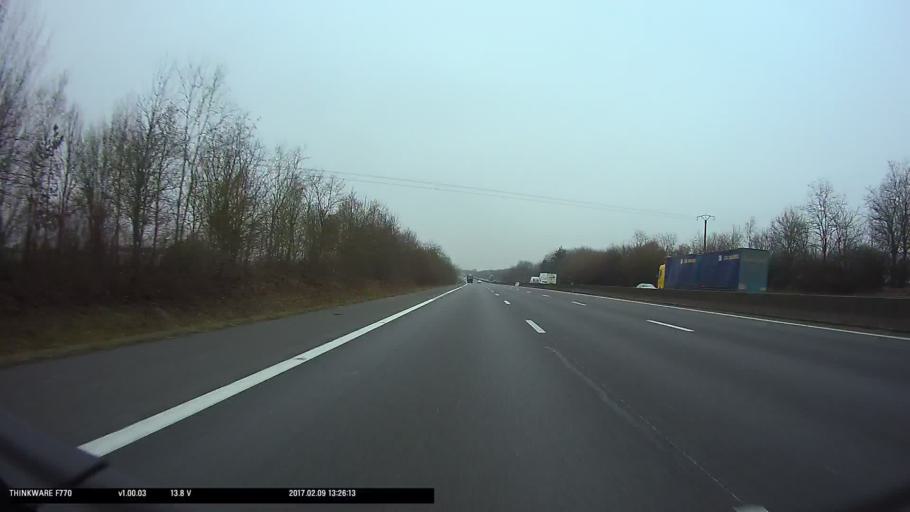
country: FR
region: Centre
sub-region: Departement d'Eure-et-Loir
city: Baigneaux
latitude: 48.1345
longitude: 1.8542
